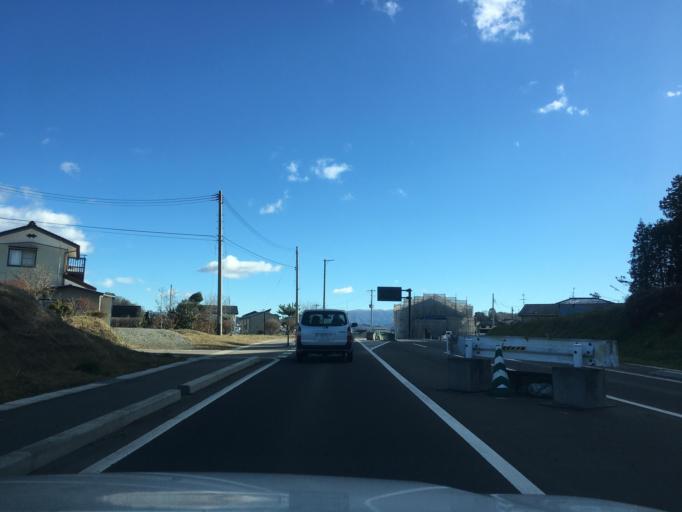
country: JP
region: Fukushima
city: Funehikimachi-funehiki
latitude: 37.4454
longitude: 140.5676
